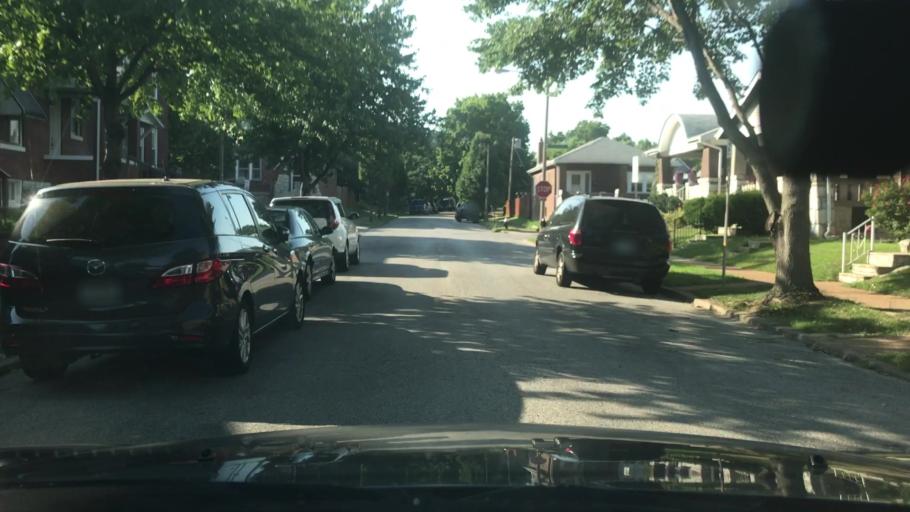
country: US
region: Missouri
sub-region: Saint Louis County
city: Lemay
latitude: 38.5780
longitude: -90.2770
